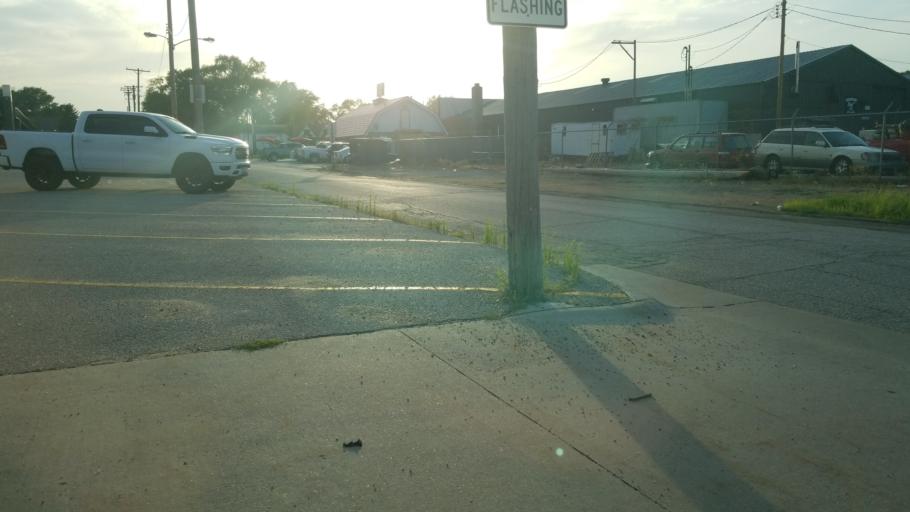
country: US
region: Nebraska
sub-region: Sarpy County
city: Papillion
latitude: 41.1534
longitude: -96.0417
